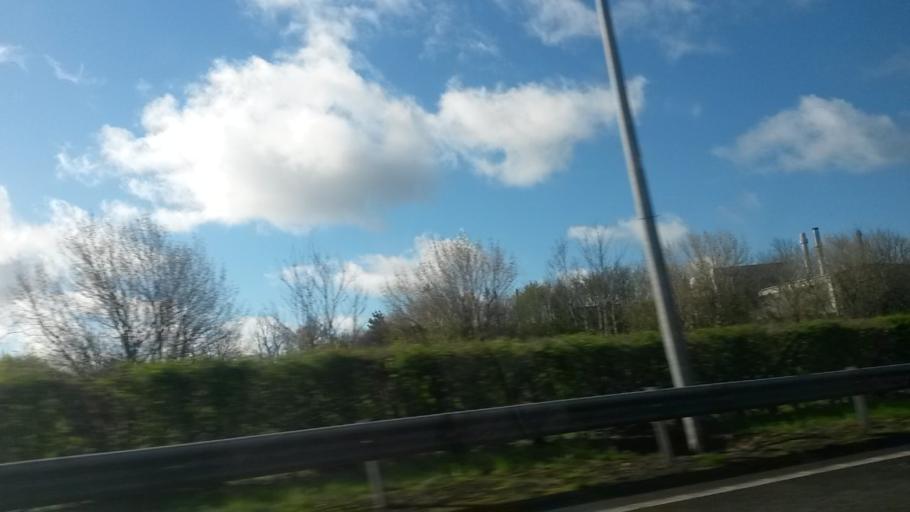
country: IE
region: Munster
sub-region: County Cork
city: Passage West
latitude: 51.9043
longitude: -8.3737
